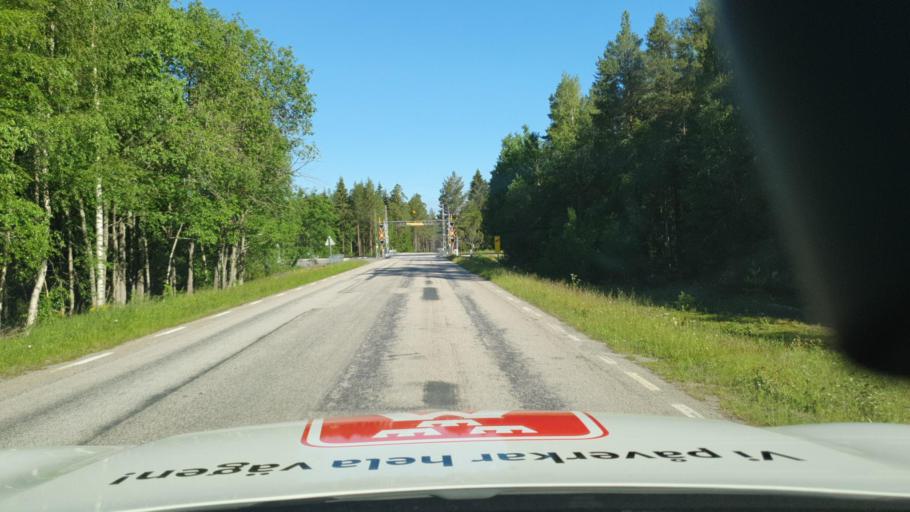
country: SE
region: Vaesterbotten
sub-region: Umea Kommun
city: Roback
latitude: 63.8561
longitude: 20.1469
